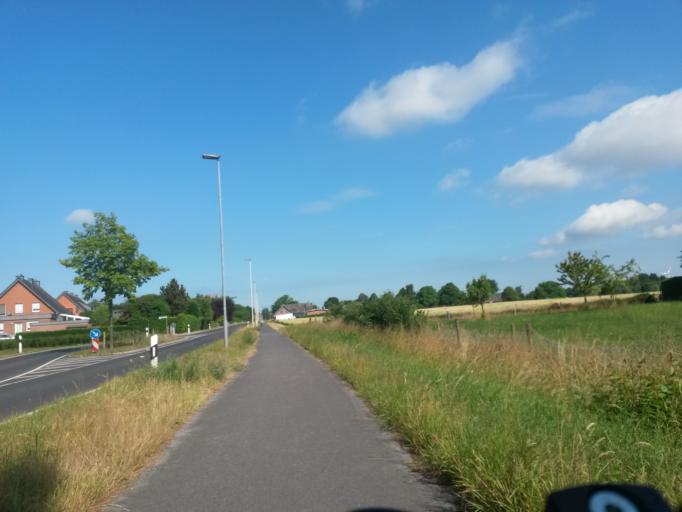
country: DE
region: North Rhine-Westphalia
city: Kempen
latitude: 51.3696
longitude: 6.3871
